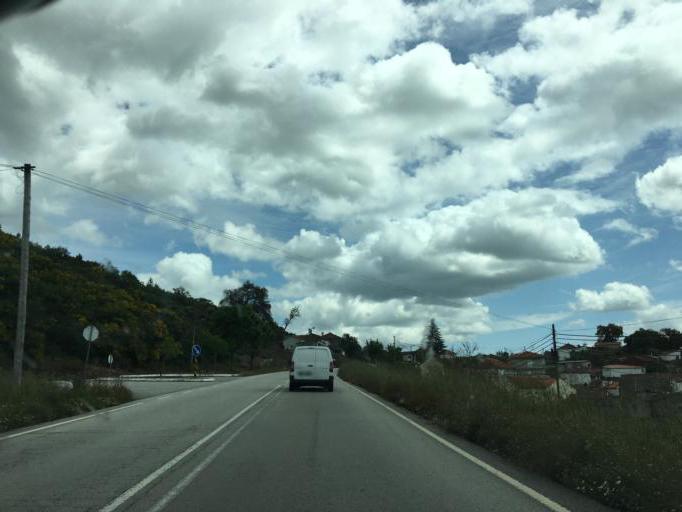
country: PT
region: Vila Real
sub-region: Boticas
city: Boticas
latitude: 41.6946
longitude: -7.6522
